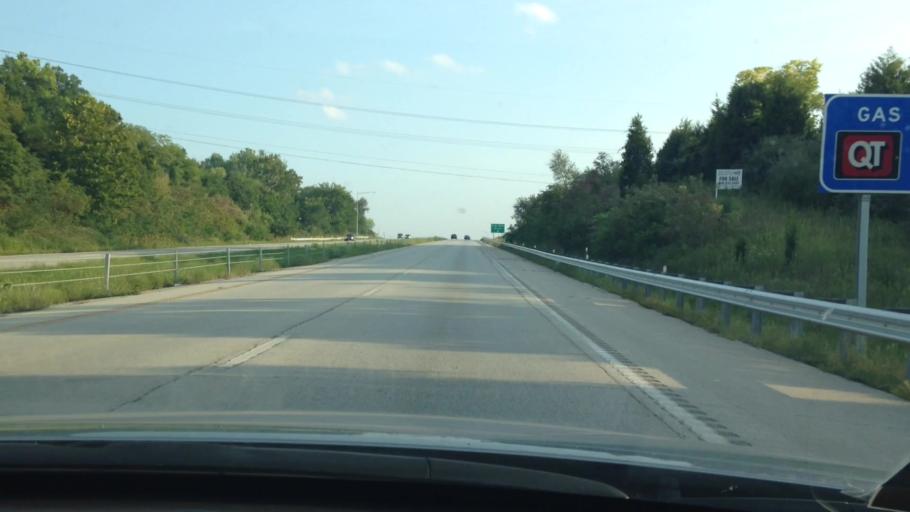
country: US
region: Missouri
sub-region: Clay County
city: Gladstone
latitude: 39.2256
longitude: -94.5894
